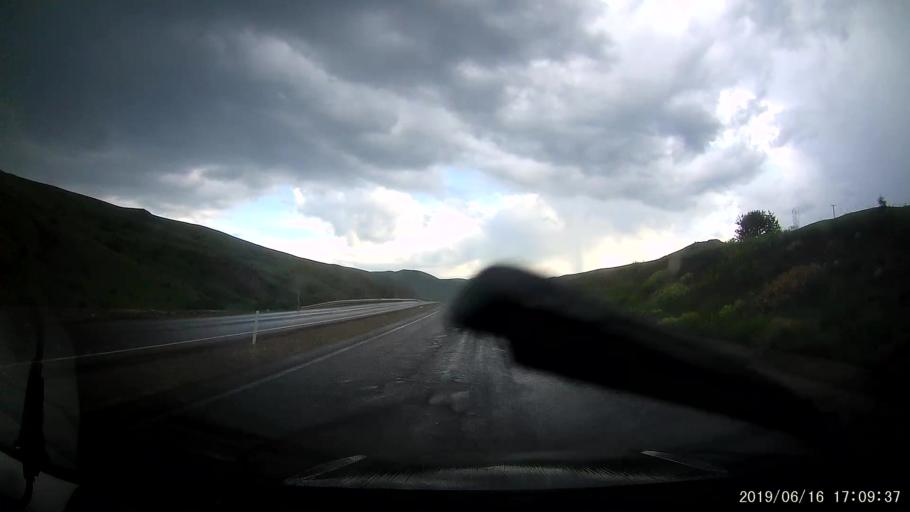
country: TR
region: Erzurum
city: Askale
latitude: 39.8923
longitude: 40.6482
